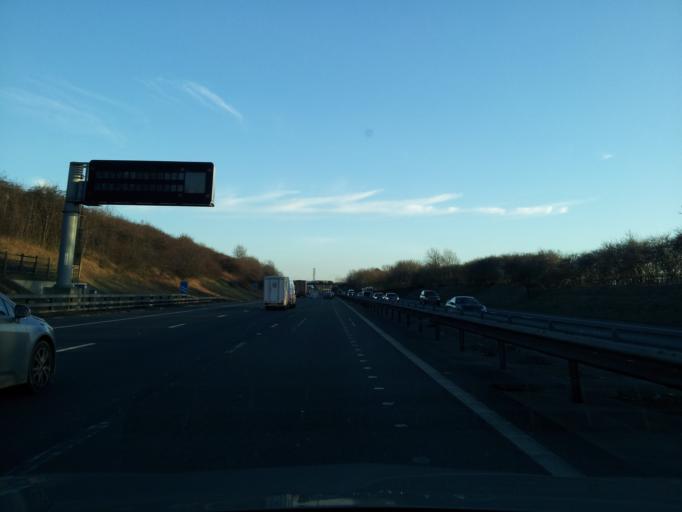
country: GB
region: England
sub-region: Milton Keynes
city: Gayhurst
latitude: 52.0876
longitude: -0.7531
